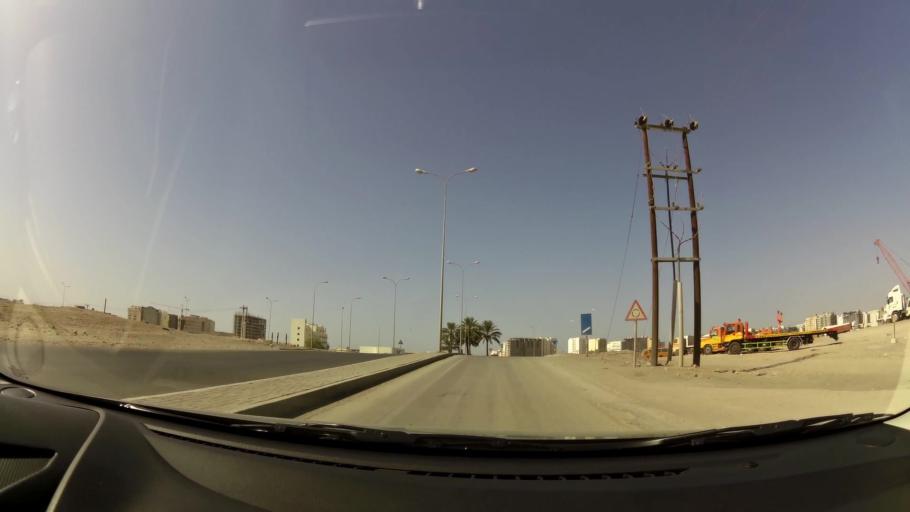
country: OM
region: Muhafazat Masqat
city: Bawshar
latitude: 23.5819
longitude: 58.3592
